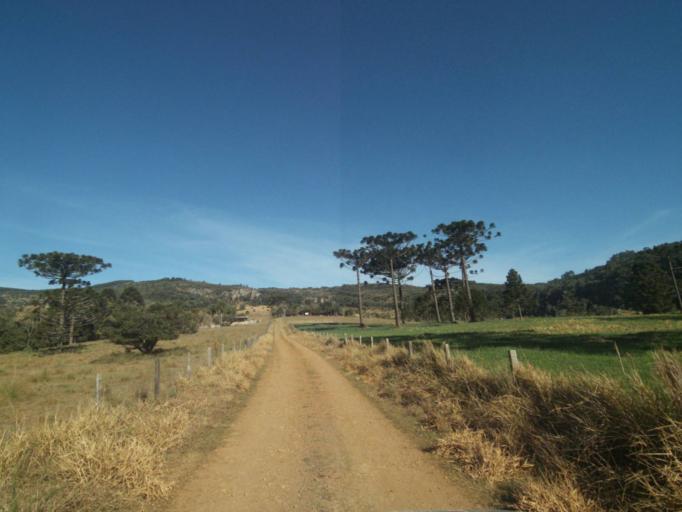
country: BR
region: Parana
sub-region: Tibagi
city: Tibagi
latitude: -24.5572
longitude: -50.5196
